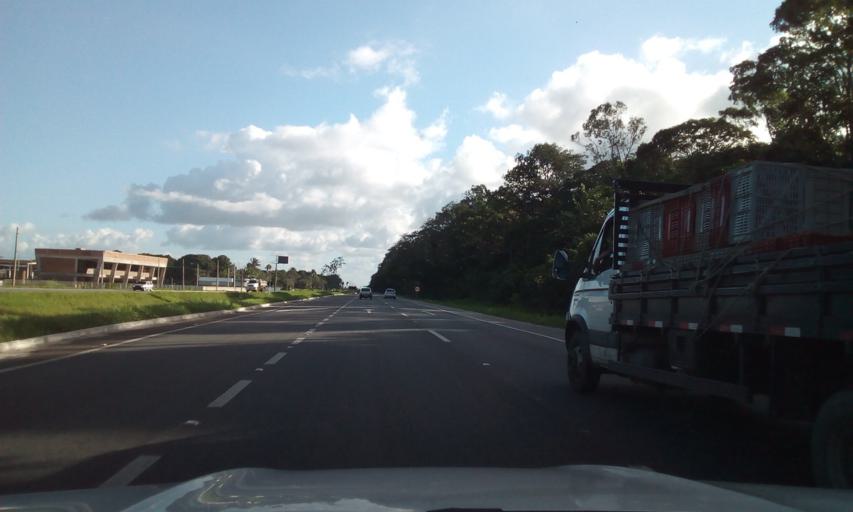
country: BR
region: Paraiba
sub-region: Santa Rita
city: Santa Rita
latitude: -7.1454
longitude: -34.9994
